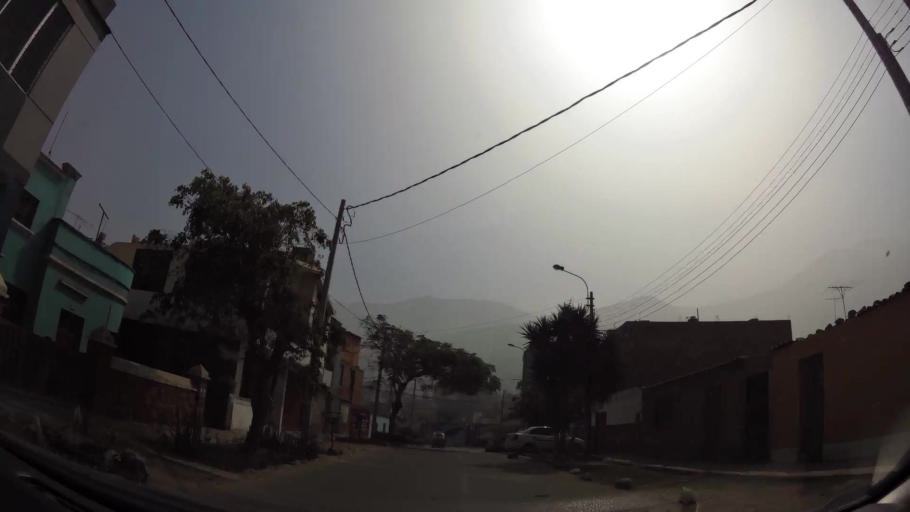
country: PE
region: Lima
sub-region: Lima
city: Asentamiento Humano Nicolas de Pierola
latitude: -11.9385
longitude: -76.6941
